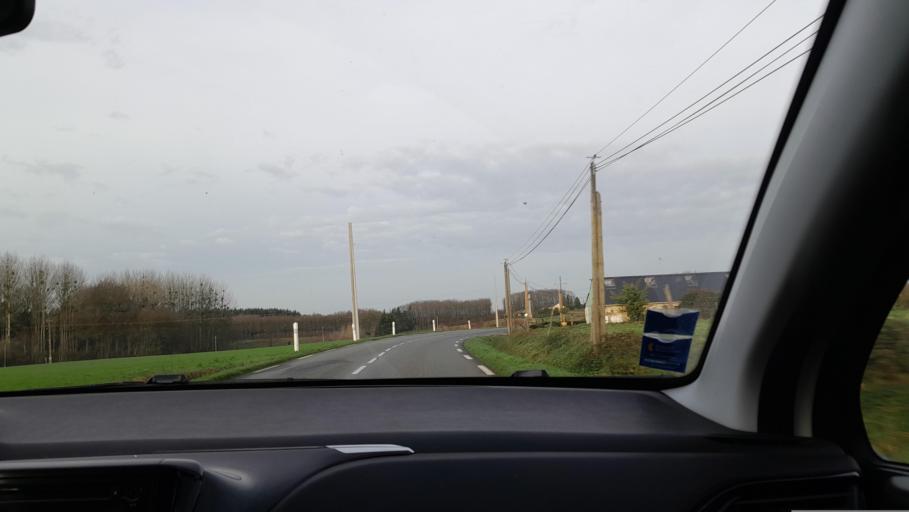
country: FR
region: Brittany
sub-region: Departement d'Ille-et-Vilaine
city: La Guerche-de-Bretagne
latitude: 47.9143
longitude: -1.2029
